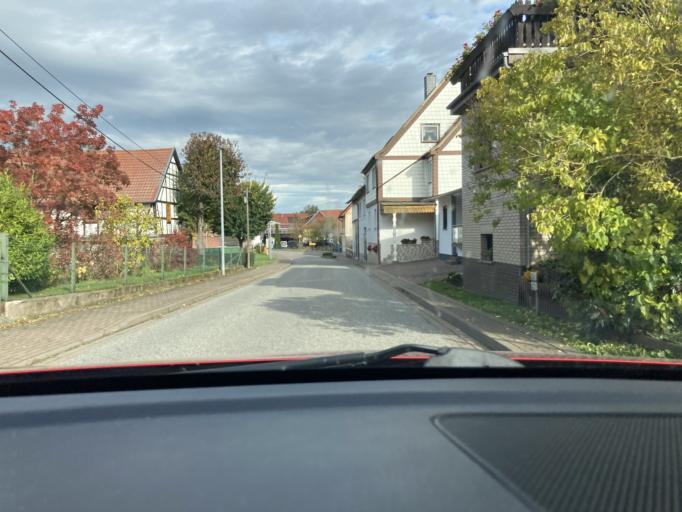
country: DE
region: Thuringia
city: Kleinbodungen
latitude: 51.5063
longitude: 10.5462
